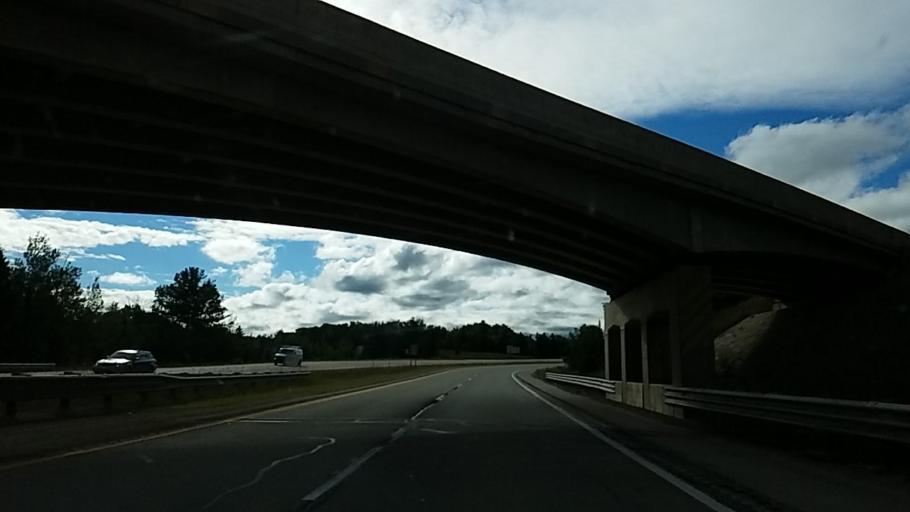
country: US
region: Michigan
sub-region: Mackinac County
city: Saint Ignace
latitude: 45.7629
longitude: -84.7324
